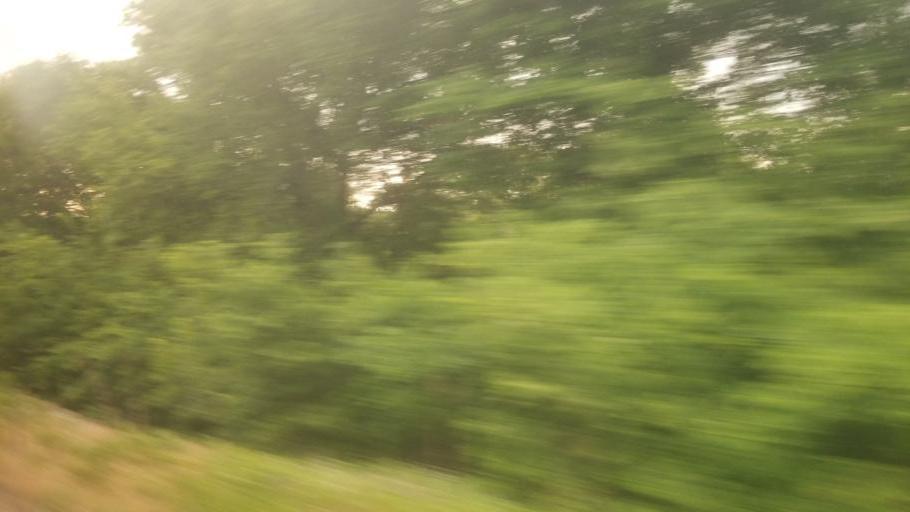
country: US
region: Kansas
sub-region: Chase County
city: Cottonwood Falls
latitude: 38.3976
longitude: -96.5831
